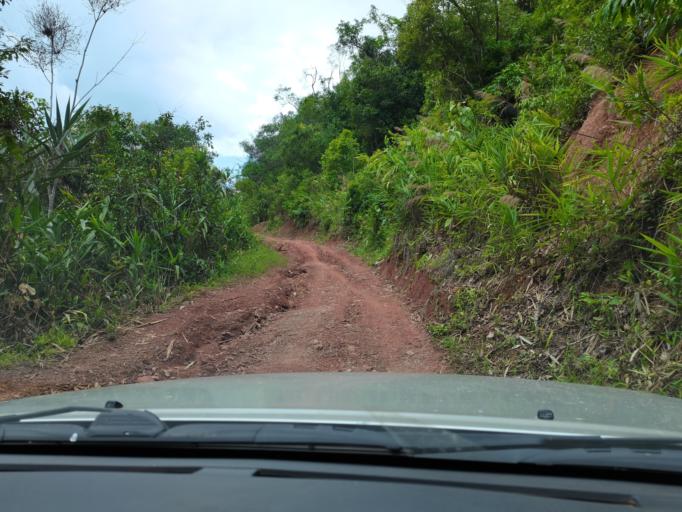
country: LA
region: Loungnamtha
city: Muang Nale
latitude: 20.5061
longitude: 101.0833
